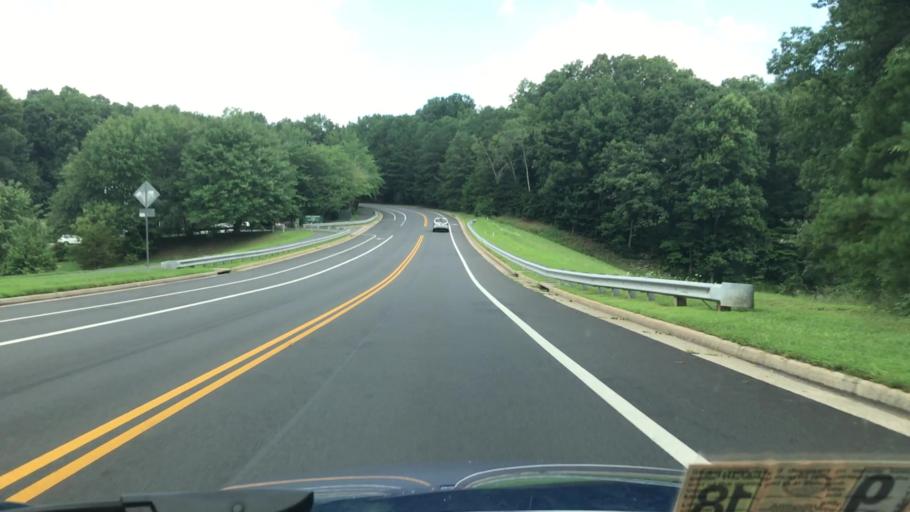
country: US
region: Virginia
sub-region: Fairfax County
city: Wolf Trap
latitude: 38.9322
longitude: -77.3250
